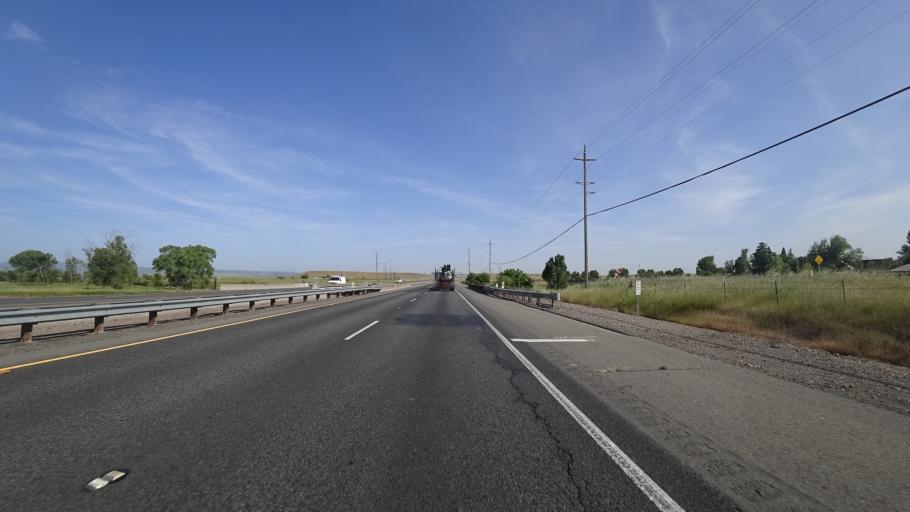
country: US
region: California
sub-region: Butte County
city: Durham
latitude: 39.6329
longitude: -121.7057
